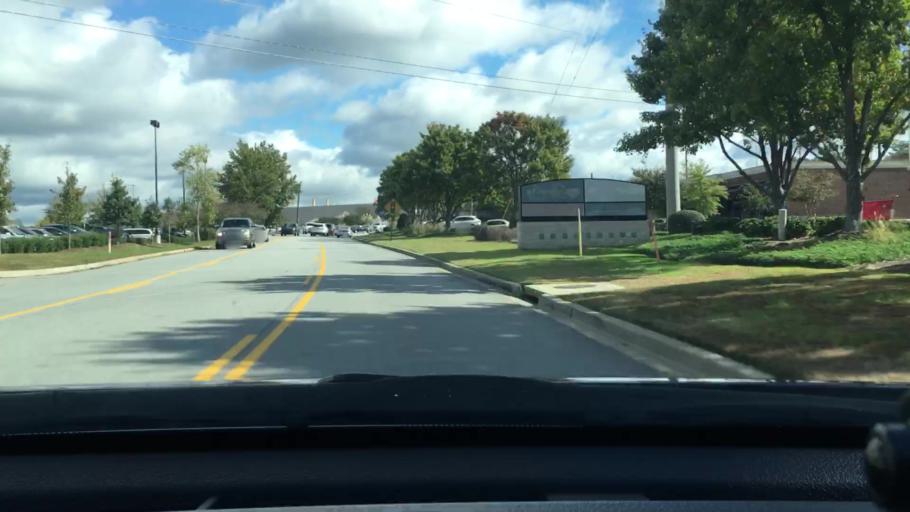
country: US
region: South Carolina
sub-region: Lexington County
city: Seven Oaks
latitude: 34.0702
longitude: -81.1538
